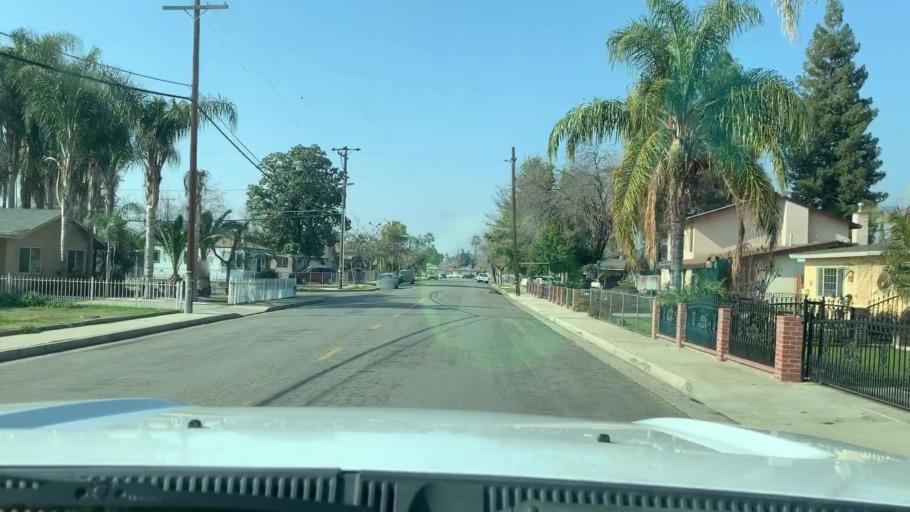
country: US
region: California
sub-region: Kern County
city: Shafter
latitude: 35.4977
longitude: -119.2732
